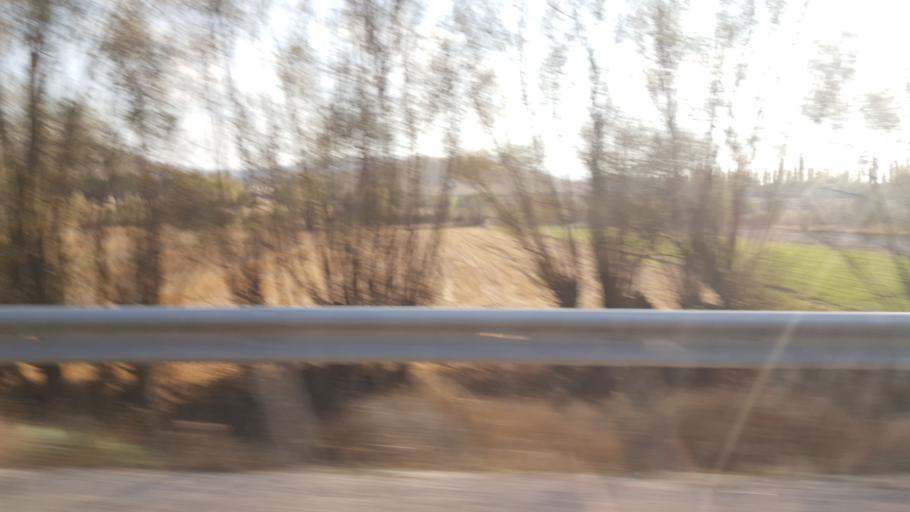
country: TR
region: Eskisehir
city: Seyitgazi
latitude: 39.4153
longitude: 30.6405
